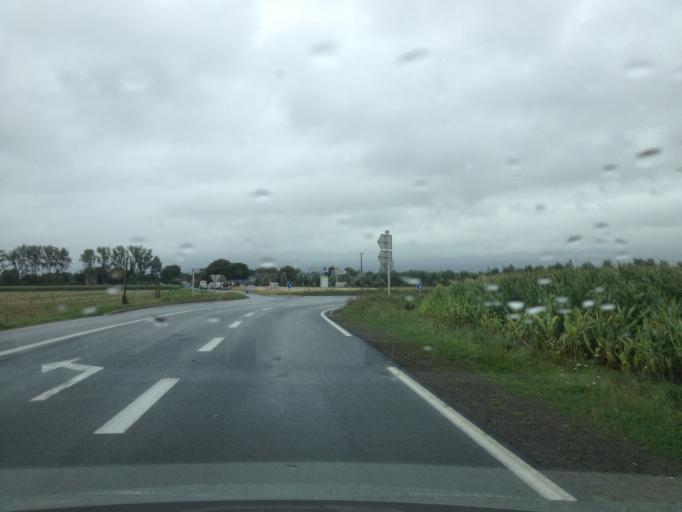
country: FR
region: Lower Normandy
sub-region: Departement de la Manche
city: Pontorson
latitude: 48.6074
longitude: -1.5105
